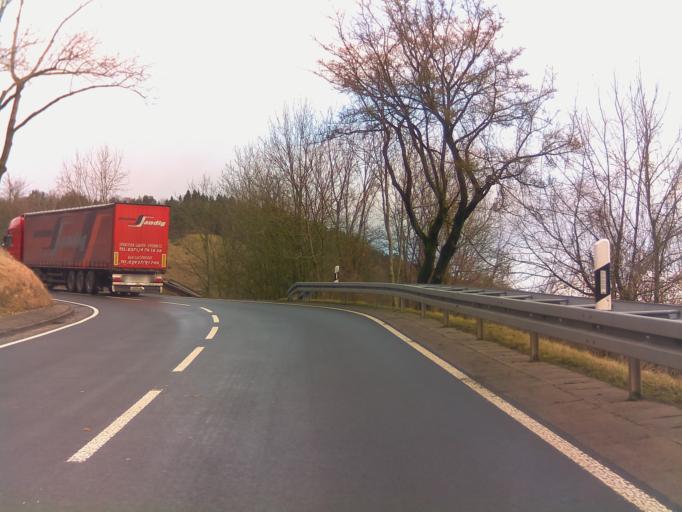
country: DE
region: Thuringia
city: Oechsen
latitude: 50.7249
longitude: 10.0884
